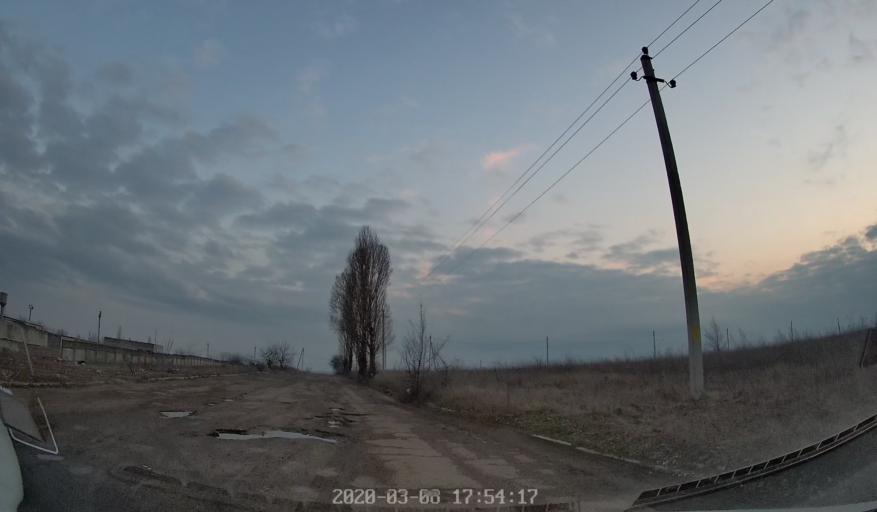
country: MD
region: Rezina
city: Rezina
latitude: 47.7534
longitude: 28.9491
